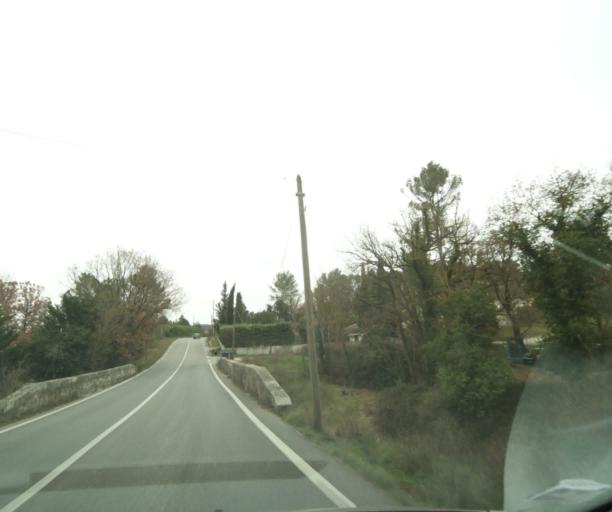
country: FR
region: Provence-Alpes-Cote d'Azur
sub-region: Departement des Bouches-du-Rhone
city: Fuveau
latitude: 43.4479
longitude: 5.5497
